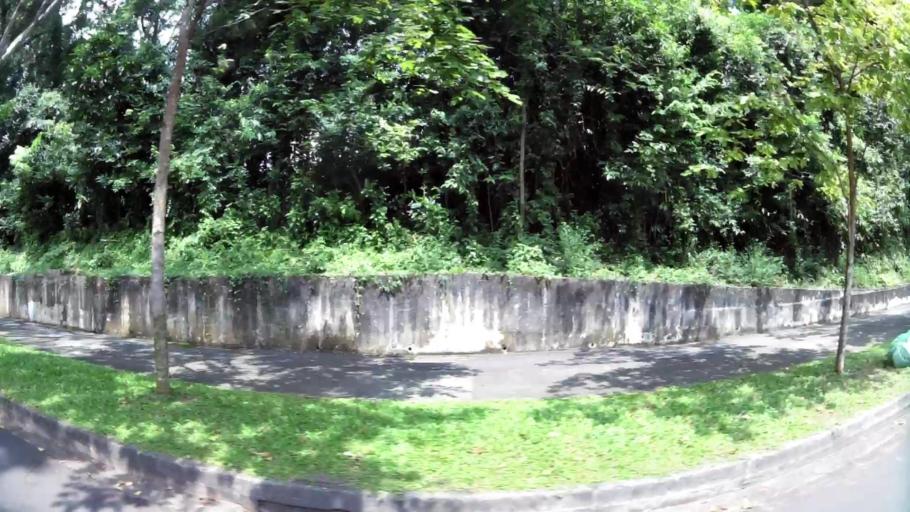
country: MY
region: Johor
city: Kampung Pasir Gudang Baru
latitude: 1.3877
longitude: 103.9784
